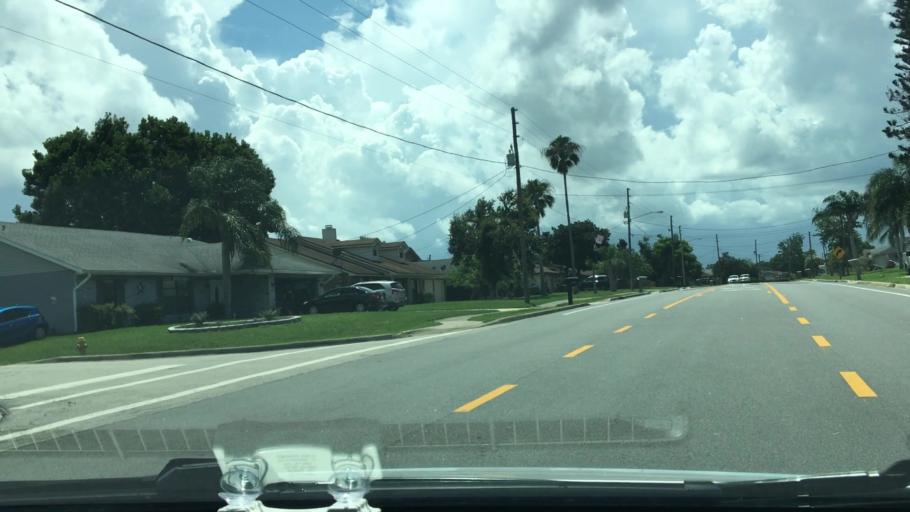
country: US
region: Florida
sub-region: Volusia County
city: Deltona
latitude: 28.8818
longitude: -81.2322
